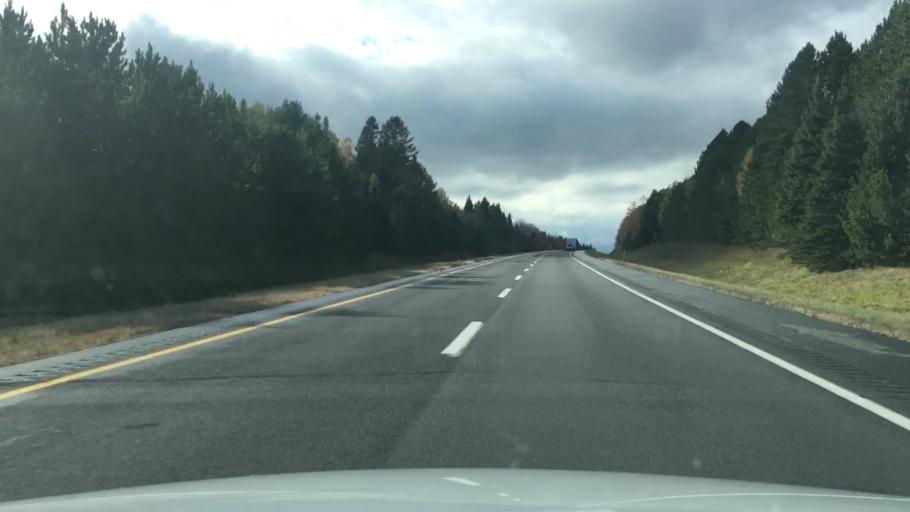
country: US
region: Maine
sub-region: Aroostook County
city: Hodgdon
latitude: 46.1406
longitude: -68.0137
